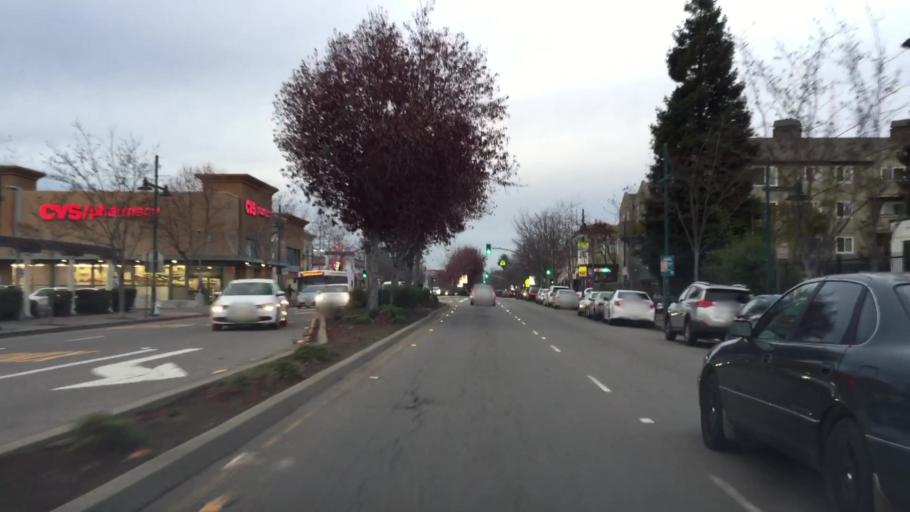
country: US
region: California
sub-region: Alameda County
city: Emeryville
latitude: 37.8333
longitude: -122.2806
